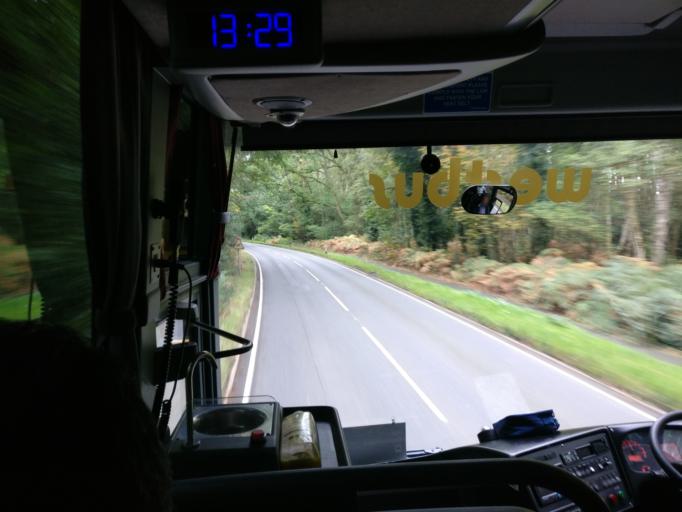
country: GB
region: England
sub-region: Surrey
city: Chobham
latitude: 51.3384
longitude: -0.5847
